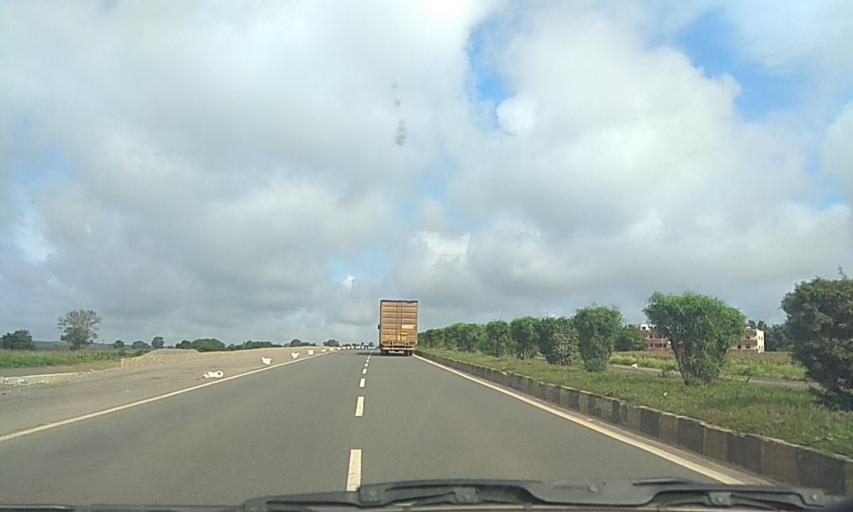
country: IN
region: Karnataka
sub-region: Haveri
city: Shiggaon
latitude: 15.0066
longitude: 75.2012
